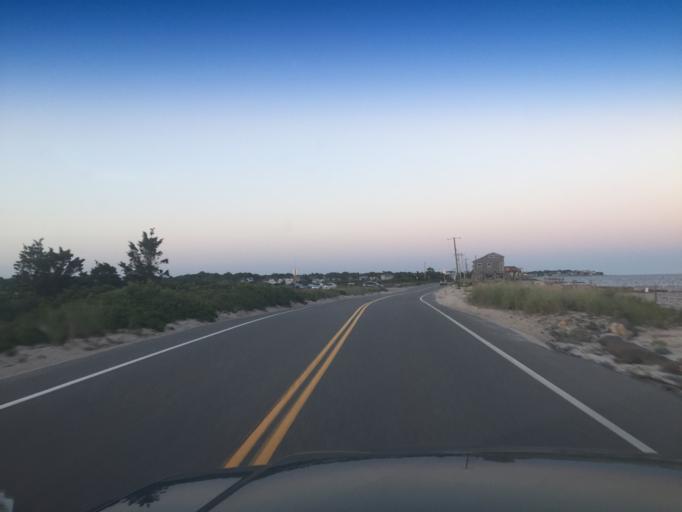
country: US
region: Massachusetts
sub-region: Barnstable County
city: Falmouth
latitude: 41.5394
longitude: -70.6315
